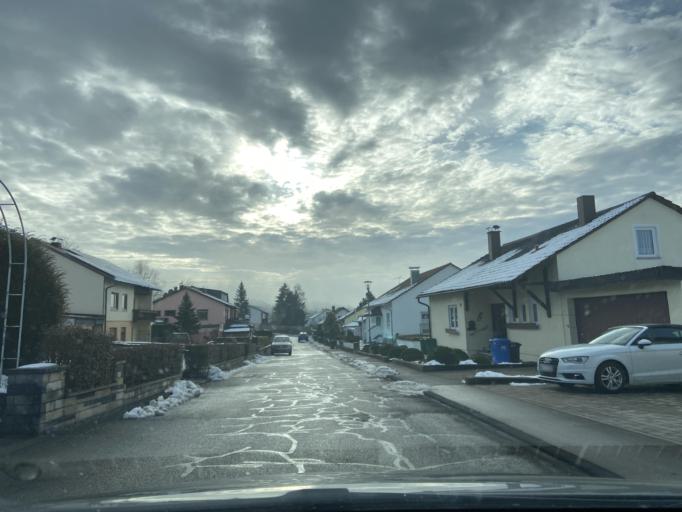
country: DE
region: Baden-Wuerttemberg
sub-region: Tuebingen Region
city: Gammertingen
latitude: 48.2517
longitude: 9.2236
